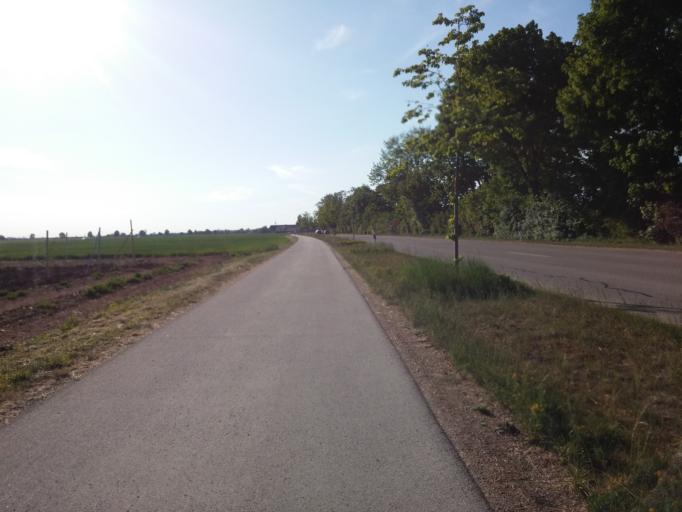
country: DE
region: Bavaria
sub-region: Upper Bavaria
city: Vaterstetten
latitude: 48.1231
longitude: 11.7517
